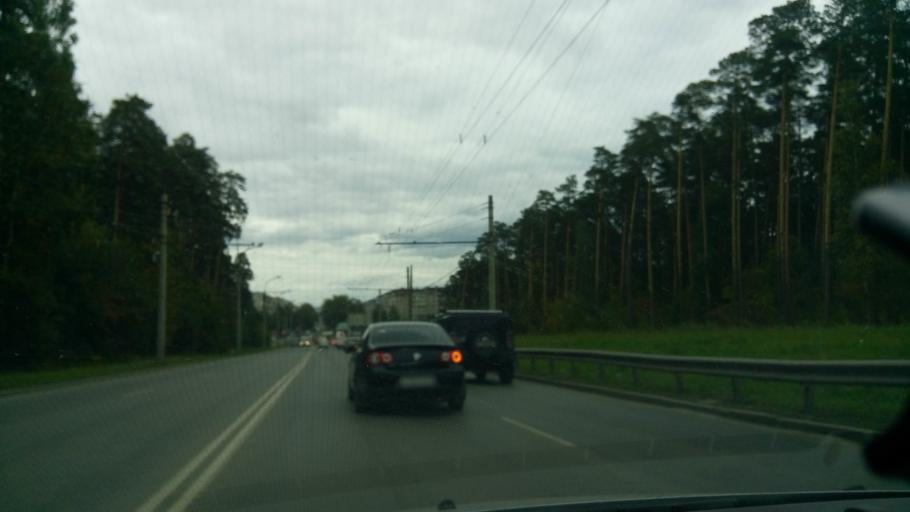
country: RU
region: Sverdlovsk
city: Sovkhoznyy
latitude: 56.7891
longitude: 60.5699
